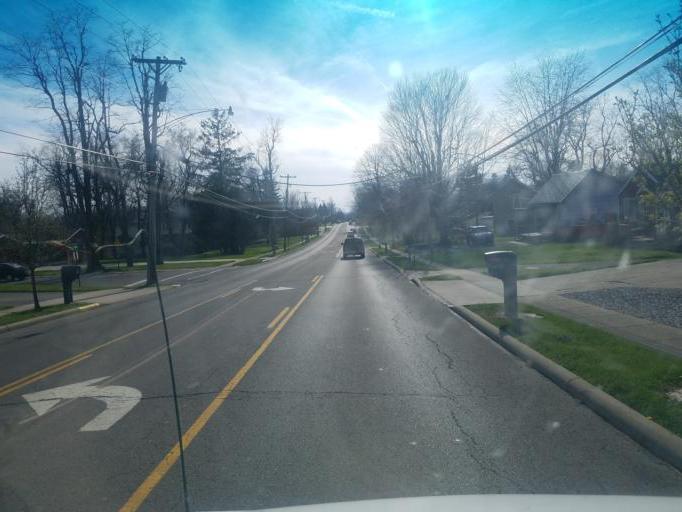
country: US
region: Ohio
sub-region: Logan County
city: Bellefontaine
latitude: 40.3651
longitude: -83.7424
